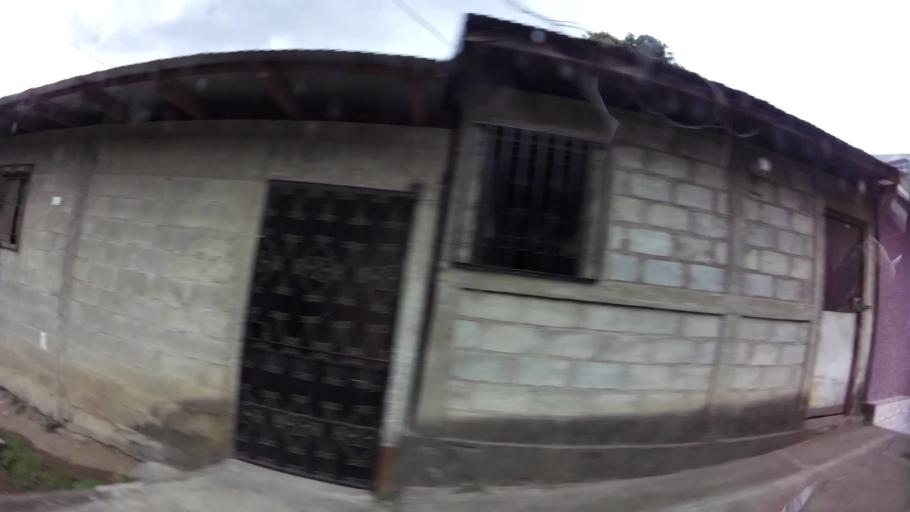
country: NI
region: Jinotega
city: Jinotega
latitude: 13.0914
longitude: -86.0046
